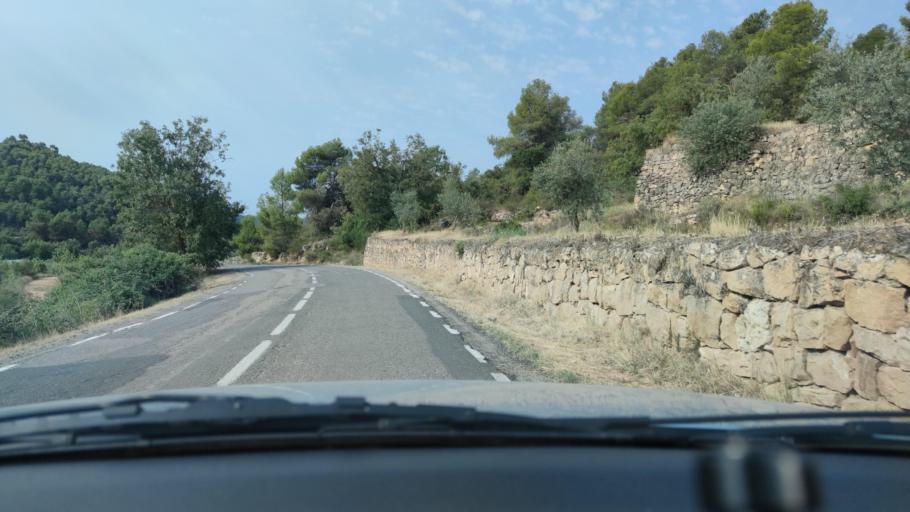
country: ES
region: Catalonia
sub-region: Provincia de Lleida
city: Juncosa
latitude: 41.4357
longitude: 0.8643
